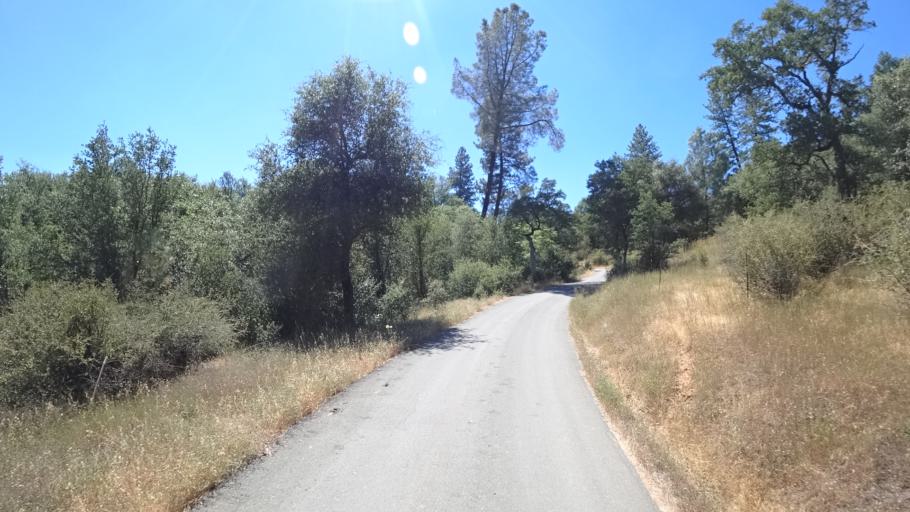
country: US
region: California
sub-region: Calaveras County
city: Mountain Ranch
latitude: 38.2993
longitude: -120.4872
